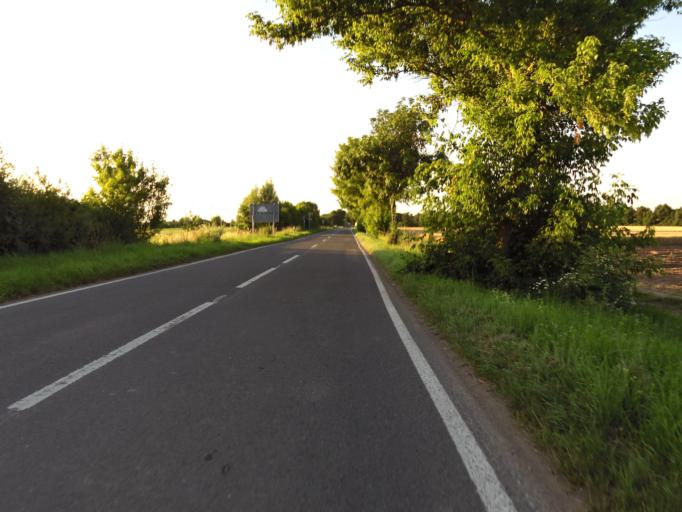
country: DE
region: Rheinland-Pfalz
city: Hessheim
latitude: 49.5590
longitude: 8.3056
